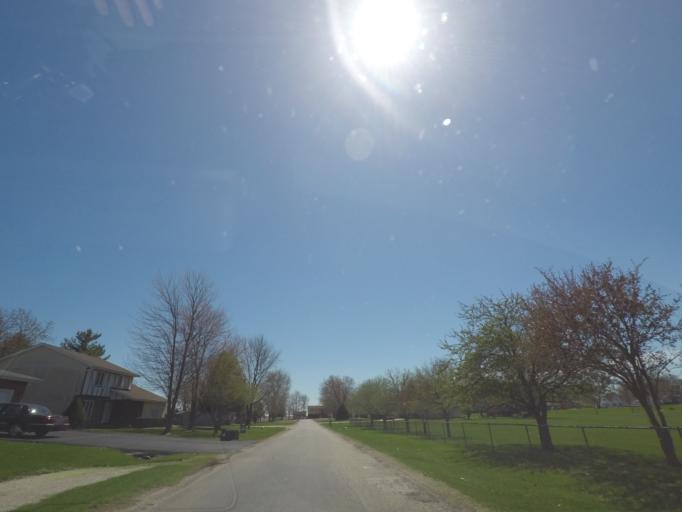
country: US
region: Illinois
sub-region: Macon County
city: Warrensburg
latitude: 39.9683
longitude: -89.1568
